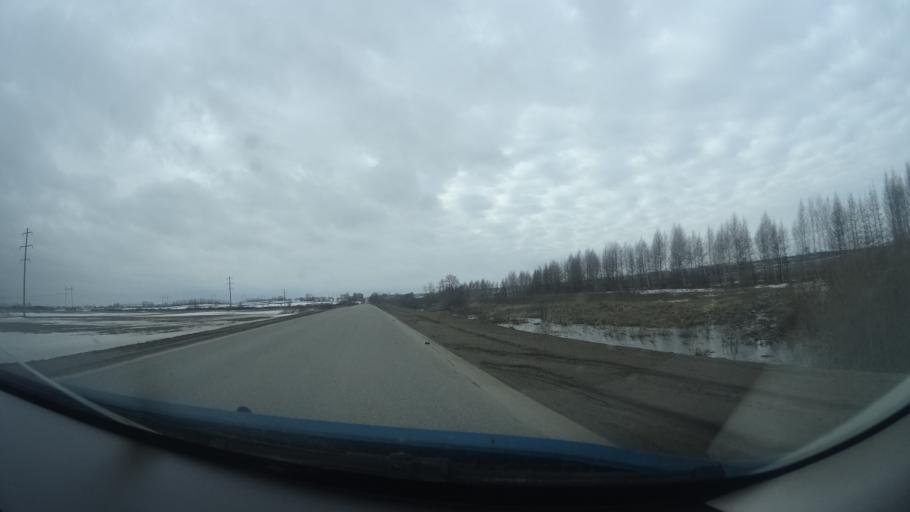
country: RU
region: Bashkortostan
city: Birsk
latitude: 55.4640
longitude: 55.5937
